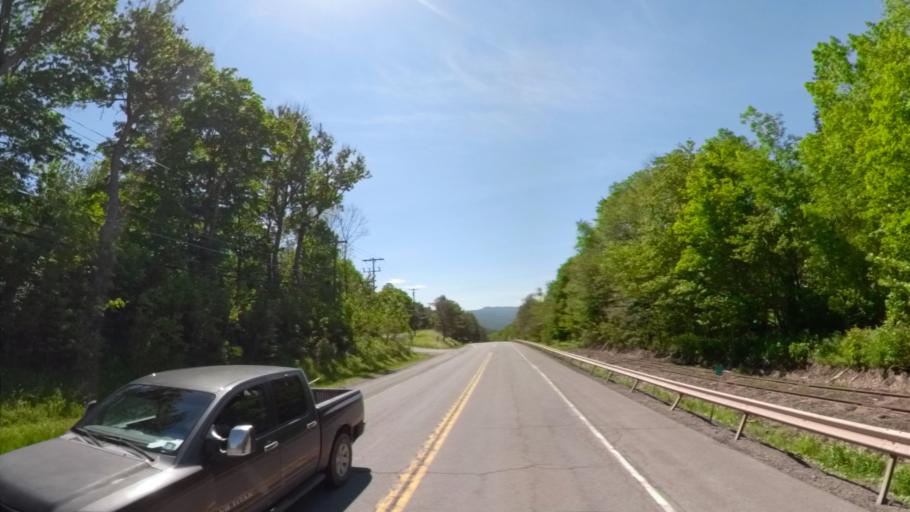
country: US
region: New York
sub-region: Delaware County
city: Stamford
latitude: 42.1453
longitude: -74.4918
